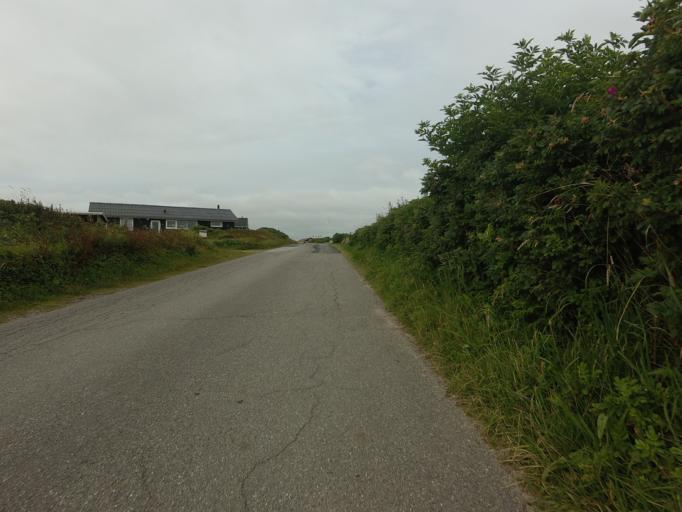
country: DK
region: North Denmark
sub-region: Jammerbugt Kommune
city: Pandrup
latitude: 57.3868
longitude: 9.7265
